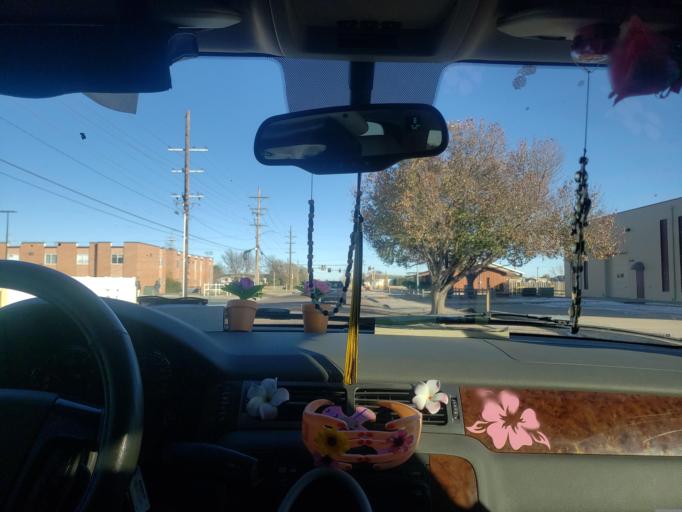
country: US
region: Kansas
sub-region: Finney County
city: Garden City
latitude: 37.9676
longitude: -100.8491
